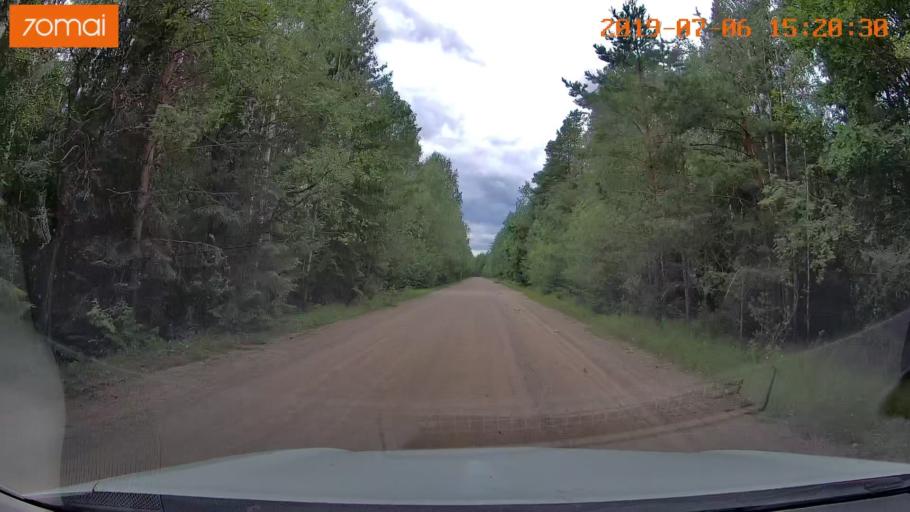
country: BY
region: Minsk
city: Valozhyn
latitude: 54.0066
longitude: 26.6337
